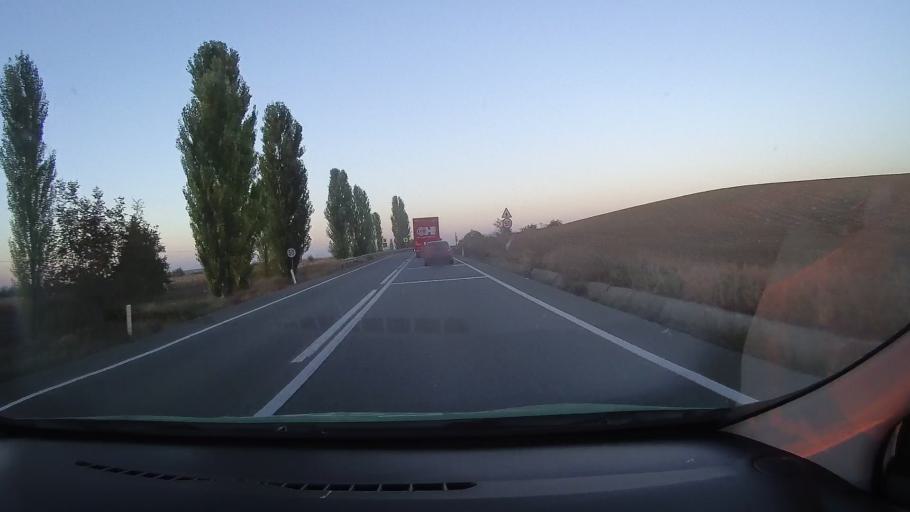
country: RO
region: Bihor
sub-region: Comuna Cherechiu
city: Cherechiu
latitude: 47.3903
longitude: 22.1467
